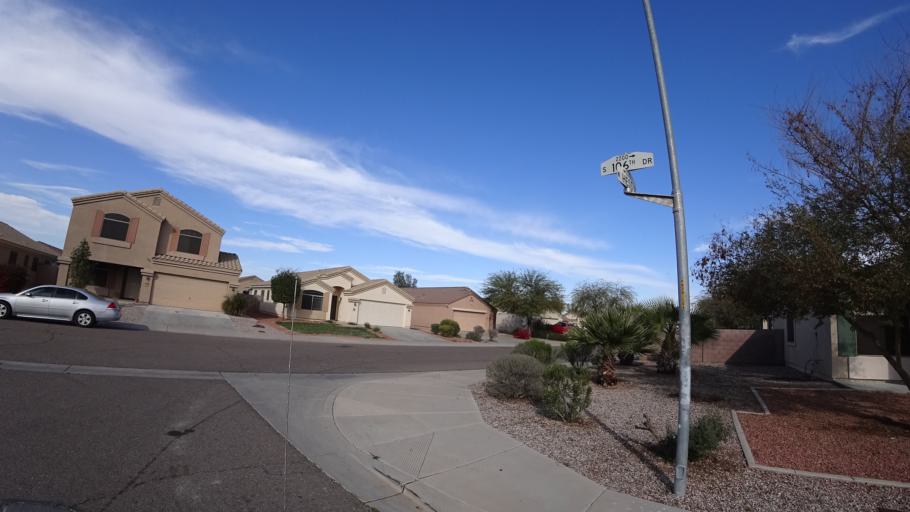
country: US
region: Arizona
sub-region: Maricopa County
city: Tolleson
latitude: 33.4268
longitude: -112.2884
